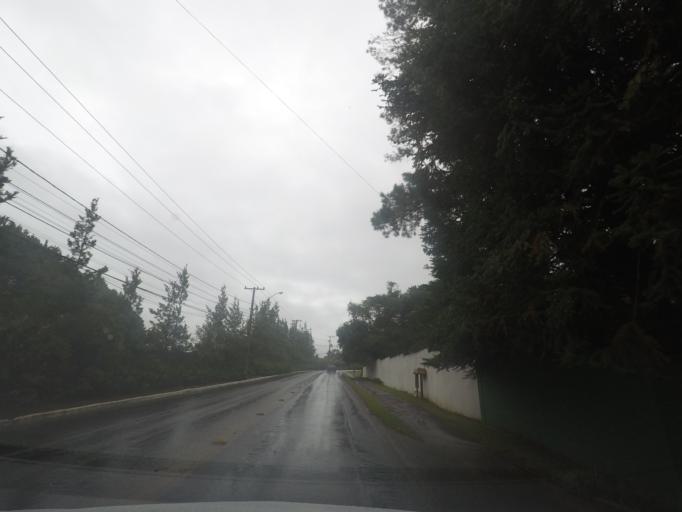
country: BR
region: Parana
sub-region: Quatro Barras
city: Quatro Barras
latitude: -25.3750
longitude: -49.1072
